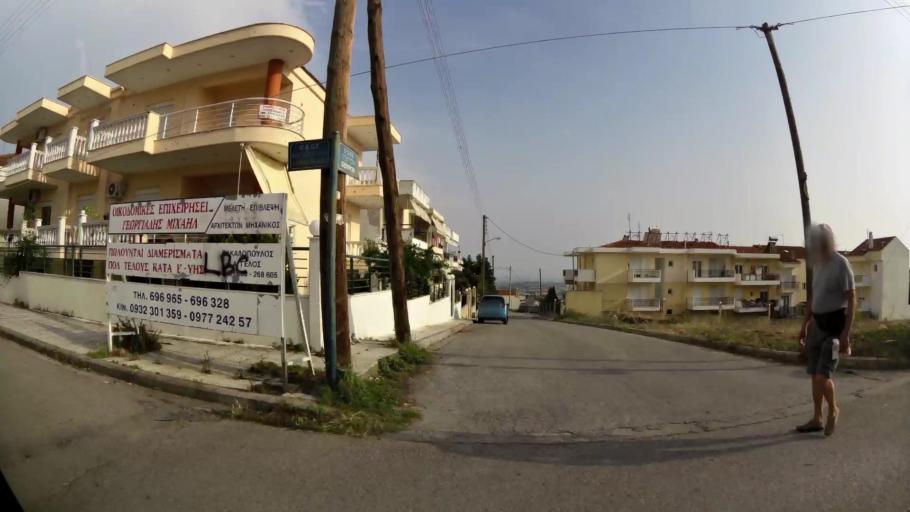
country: GR
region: Central Macedonia
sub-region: Nomos Thessalonikis
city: Oraiokastro
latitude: 40.7208
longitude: 22.9116
